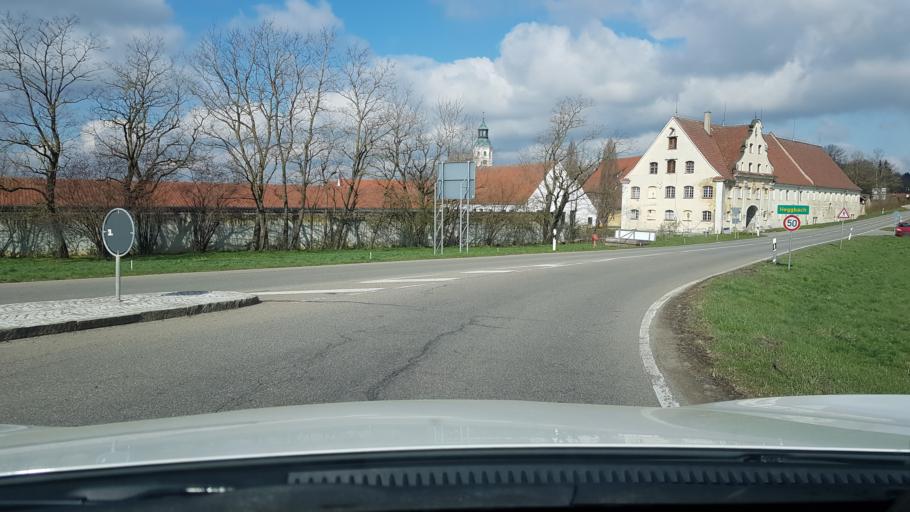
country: DE
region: Baden-Wuerttemberg
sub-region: Tuebingen Region
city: Maselheim
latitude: 48.1495
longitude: 9.8995
